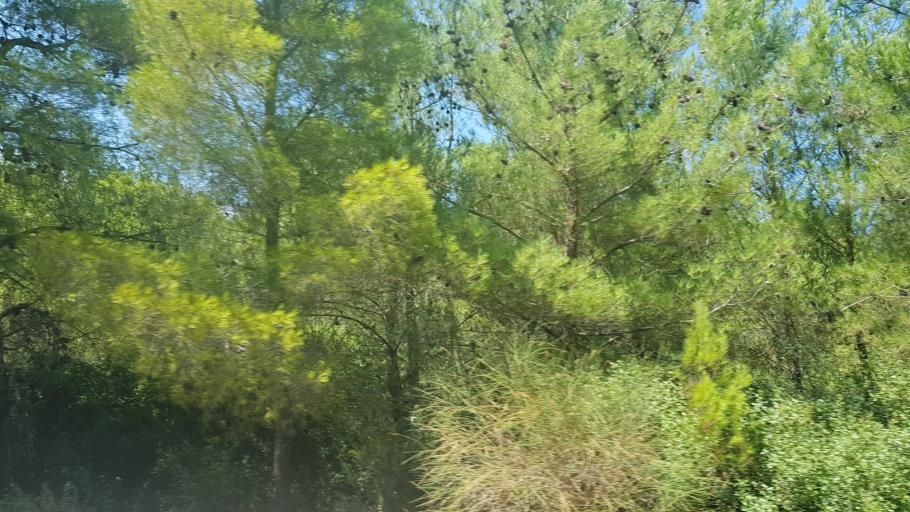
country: TR
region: Izmir
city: Urla
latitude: 38.2315
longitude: 26.6907
